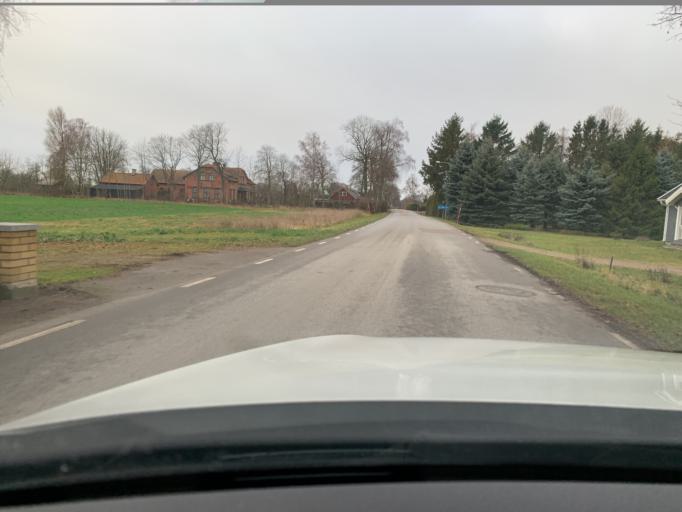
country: SE
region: Skane
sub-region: Kavlinge Kommun
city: Hofterup
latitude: 55.8379
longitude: 13.0042
